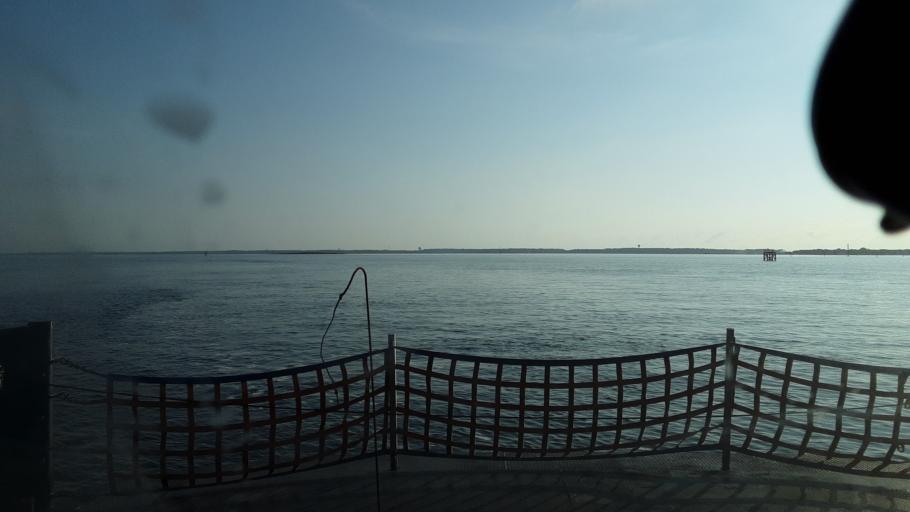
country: US
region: North Carolina
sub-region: New Hanover County
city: Kure Beach
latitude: 33.9603
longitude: -77.9534
